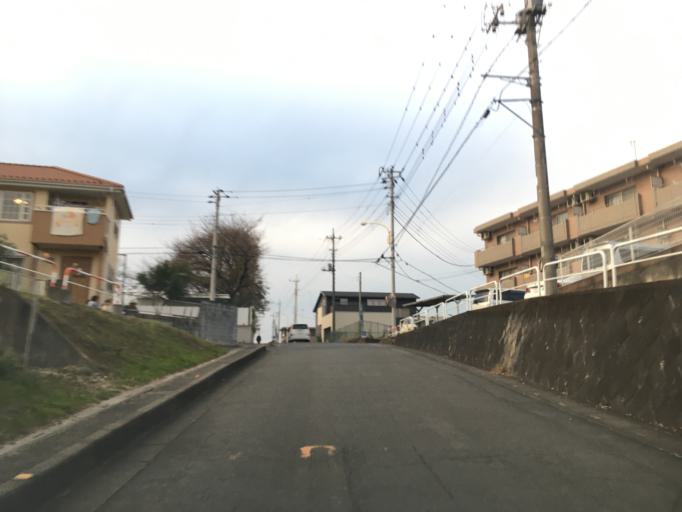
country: JP
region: Saitama
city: Sayama
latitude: 35.8973
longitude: 139.3755
